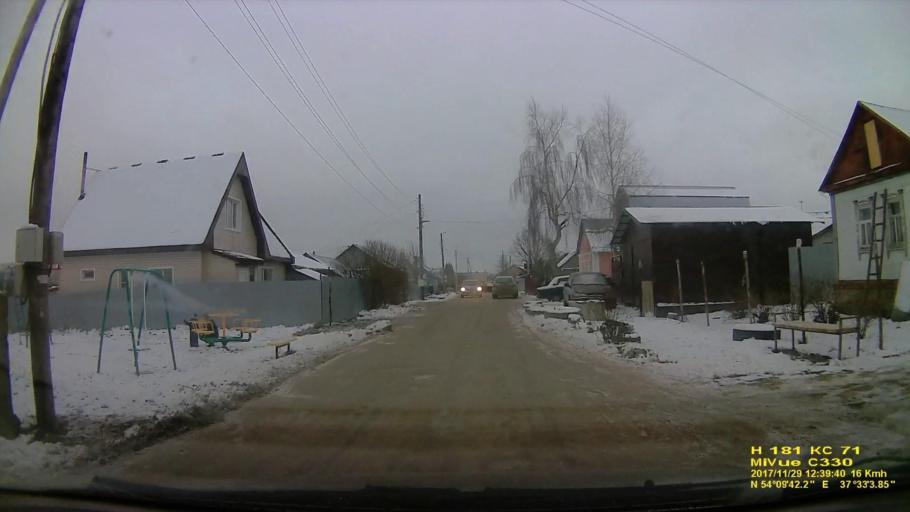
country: RU
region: Tula
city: Kosaya Gora
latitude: 54.1617
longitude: 37.5511
